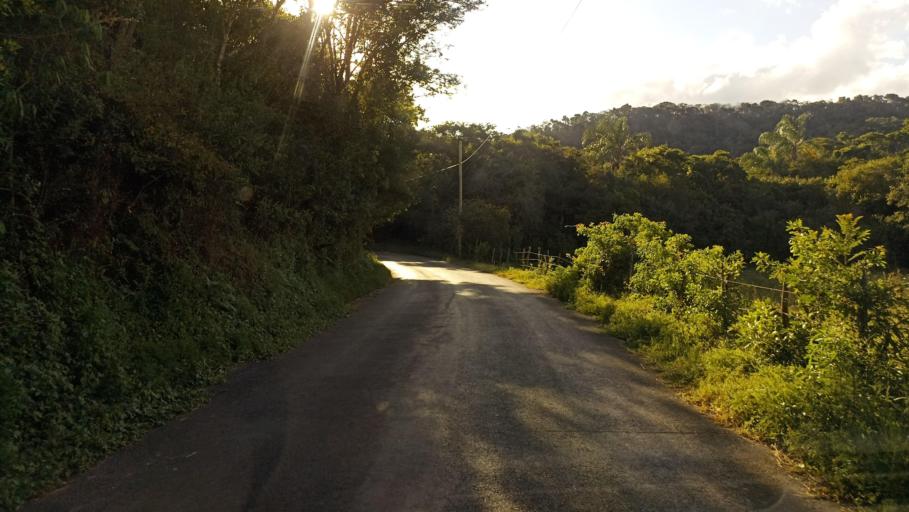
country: BR
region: Minas Gerais
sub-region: Ouro Preto
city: Ouro Preto
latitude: -20.3104
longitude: -43.6056
